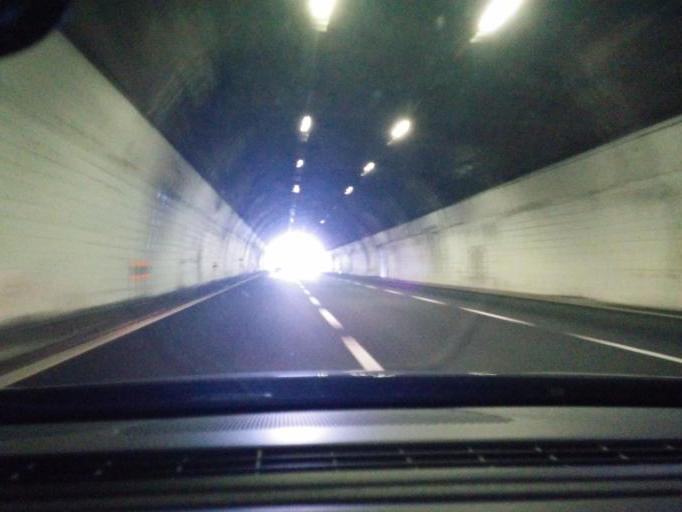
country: IT
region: Liguria
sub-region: Provincia di Genova
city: Sciarborasca
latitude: 44.3810
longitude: 8.6215
